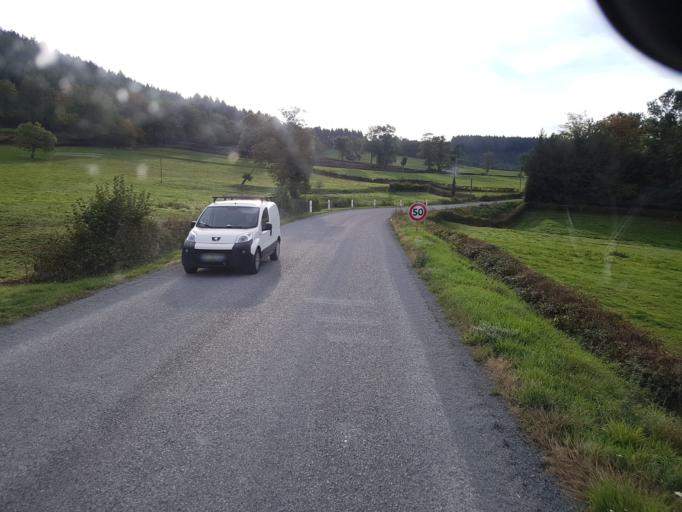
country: FR
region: Bourgogne
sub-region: Departement de Saone-et-Loire
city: Chauffailles
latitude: 46.2596
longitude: 4.4020
